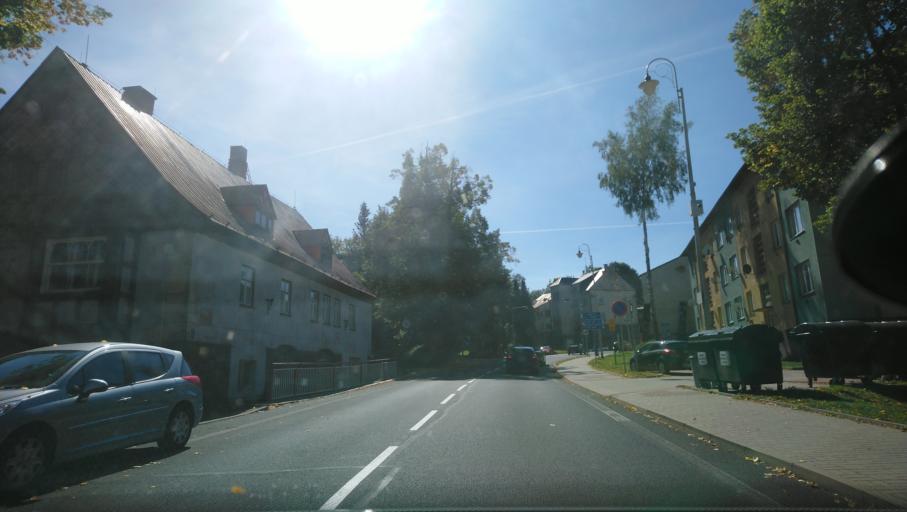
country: CZ
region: Ustecky
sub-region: Okres Chomutov
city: Vejprty
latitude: 50.4930
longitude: 13.0302
